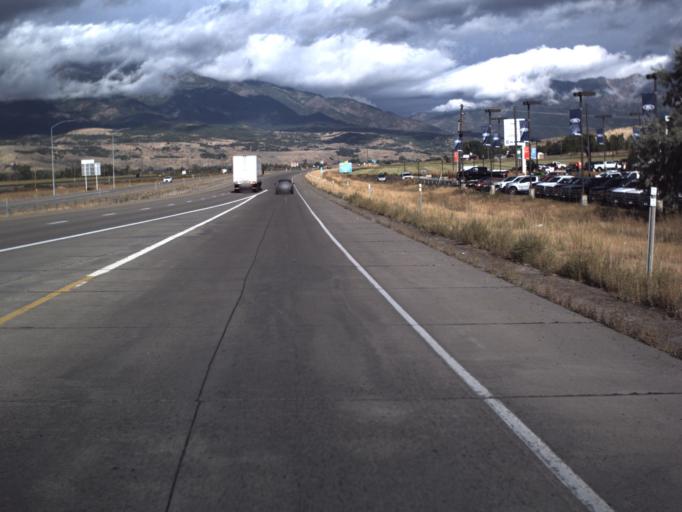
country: US
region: Utah
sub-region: Morgan County
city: Morgan
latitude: 41.0482
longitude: -111.6772
